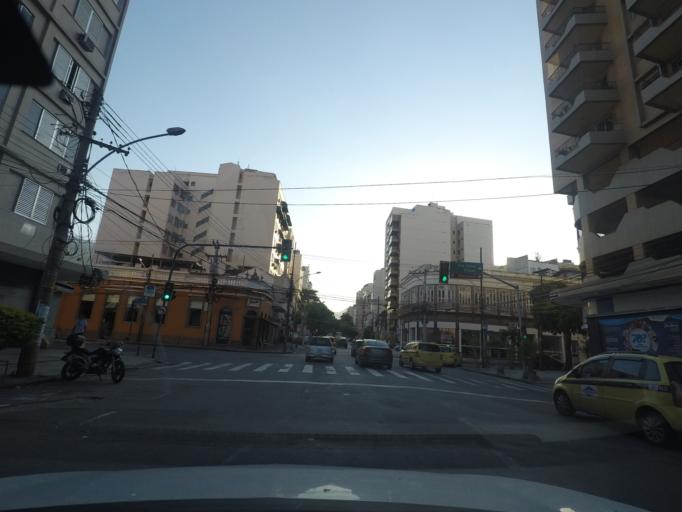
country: BR
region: Rio de Janeiro
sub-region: Rio De Janeiro
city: Rio de Janeiro
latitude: -22.9162
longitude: -43.2219
